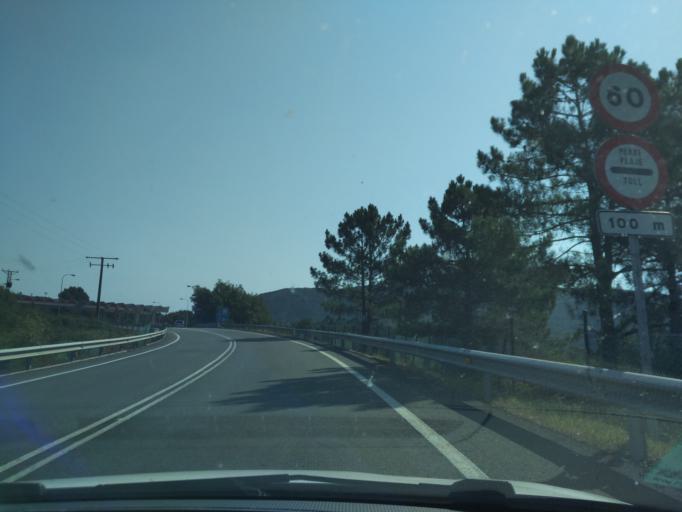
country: ES
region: Galicia
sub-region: Provincia da Coruna
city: Padron
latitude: 42.7313
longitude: -8.6423
